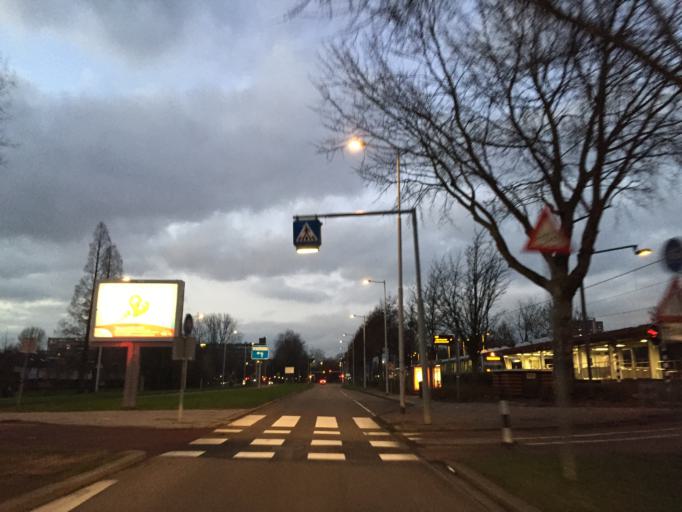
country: NL
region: South Holland
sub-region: Gemeente Rotterdam
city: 's-Gravenland
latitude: 51.9564
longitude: 4.5495
